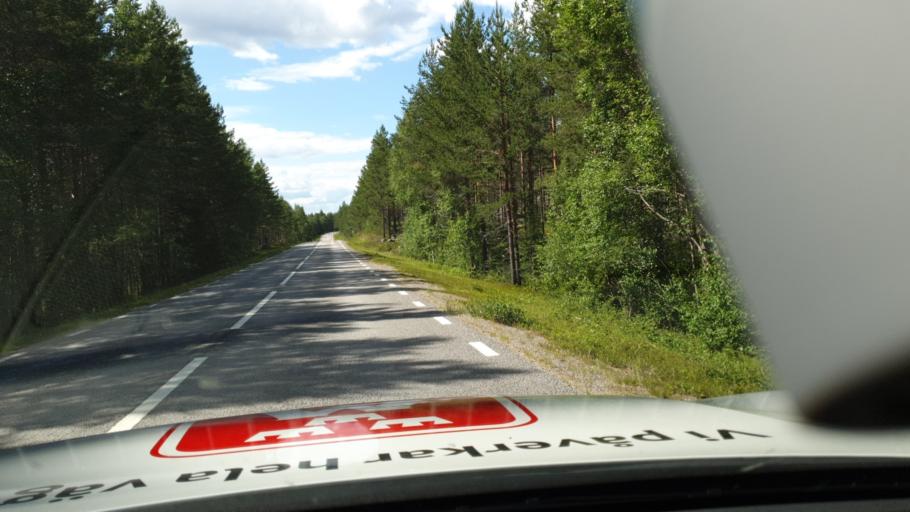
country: SE
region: Jaemtland
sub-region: Harjedalens Kommun
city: Sveg
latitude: 62.0277
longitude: 14.7989
